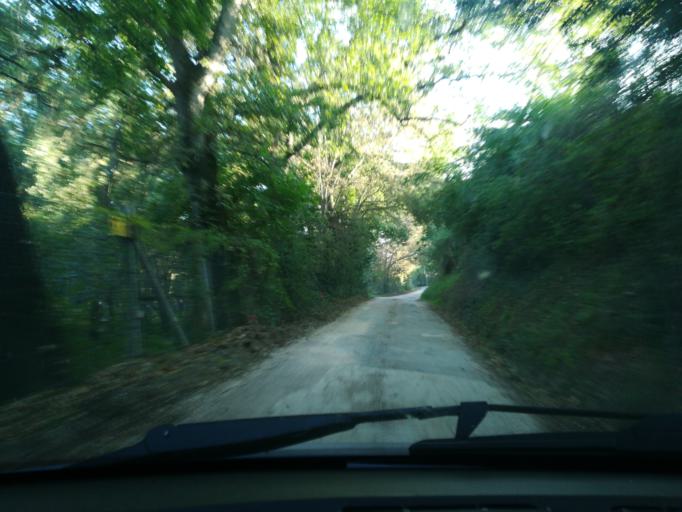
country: IT
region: The Marches
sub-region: Provincia di Macerata
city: Macerata
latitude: 43.2827
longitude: 13.4536
